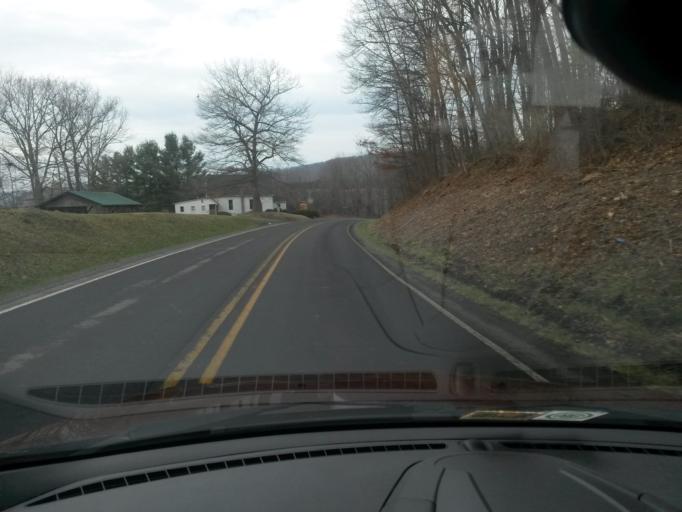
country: US
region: Virginia
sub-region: Bath County
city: Warm Springs
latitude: 38.0786
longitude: -79.7827
